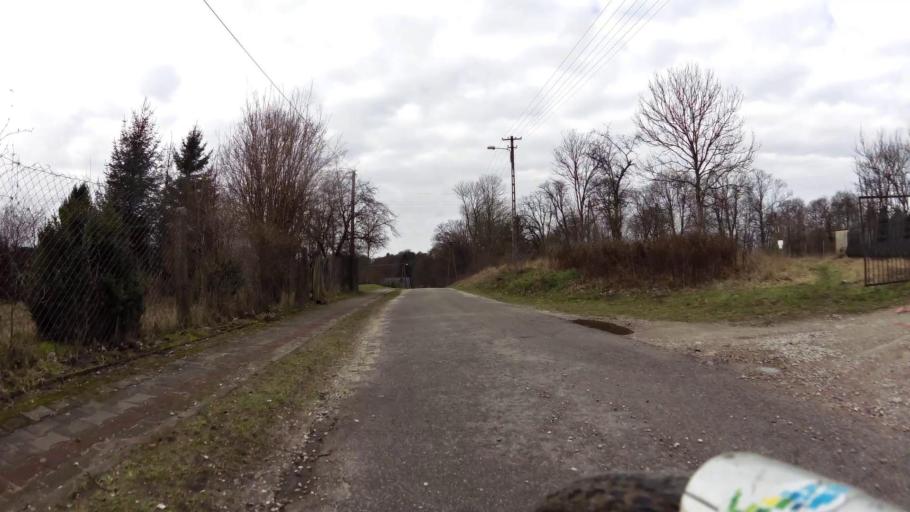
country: PL
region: Pomeranian Voivodeship
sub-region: Powiat bytowski
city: Kolczyglowy
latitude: 54.2403
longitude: 17.2443
